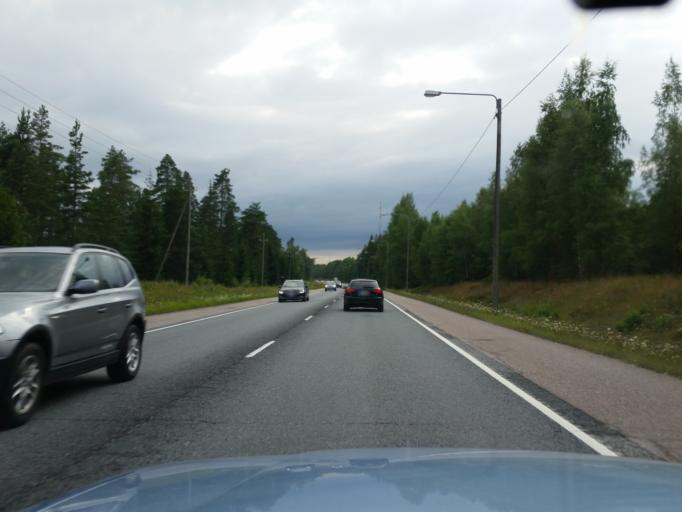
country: FI
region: Uusimaa
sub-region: Raaseporin
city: Ekenaes
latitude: 60.0004
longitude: 23.5164
